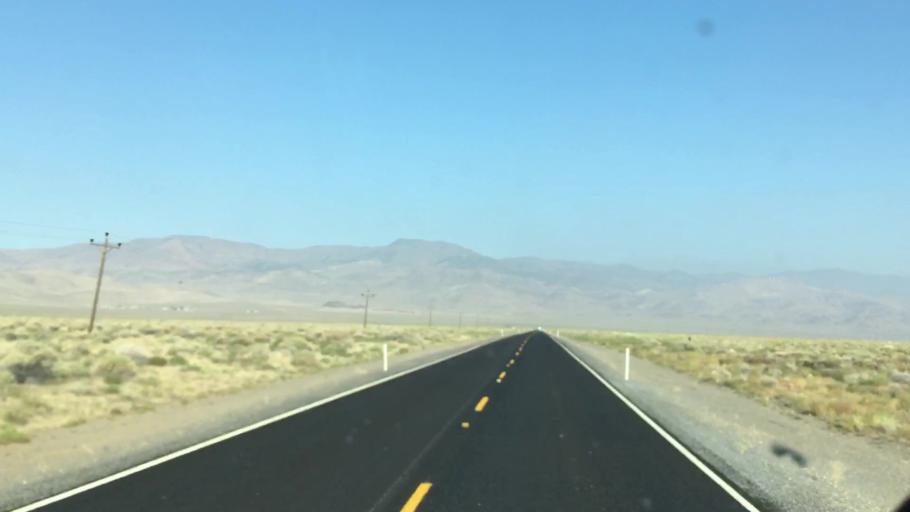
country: US
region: Nevada
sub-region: Lyon County
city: Fernley
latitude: 39.6444
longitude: -119.3078
